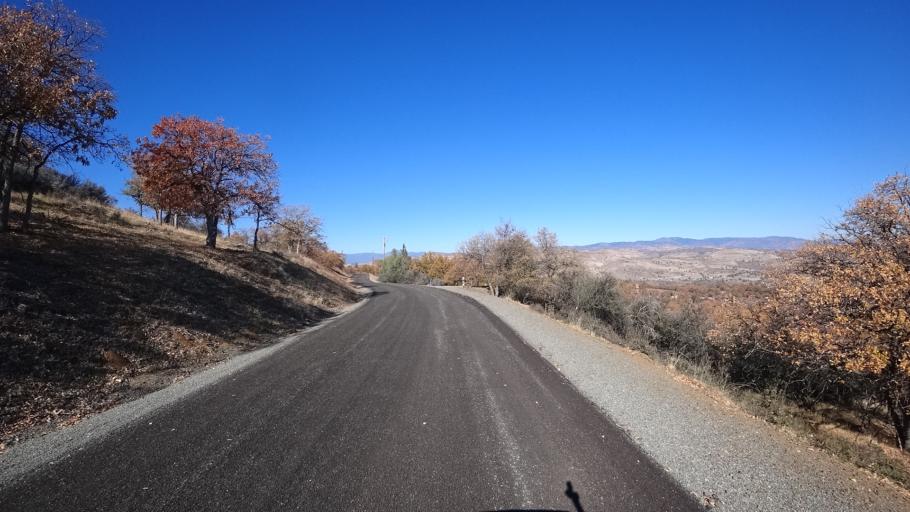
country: US
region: California
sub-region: Siskiyou County
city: Montague
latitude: 41.8761
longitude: -122.4891
